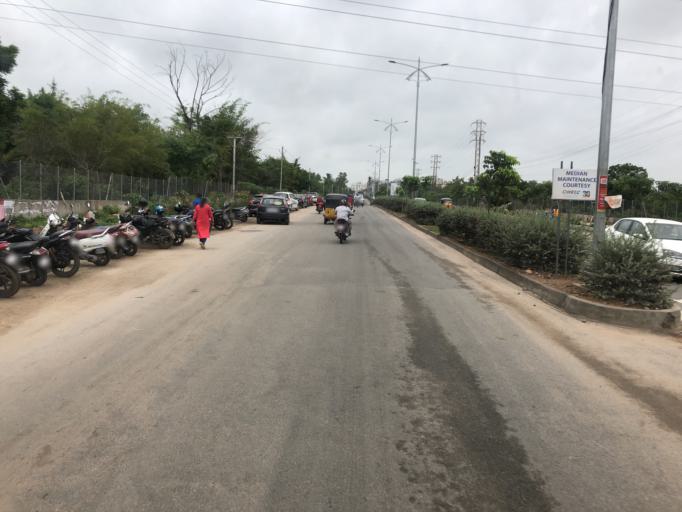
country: IN
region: Telangana
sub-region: Rangareddi
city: Kukatpalli
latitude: 17.4568
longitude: 78.3611
